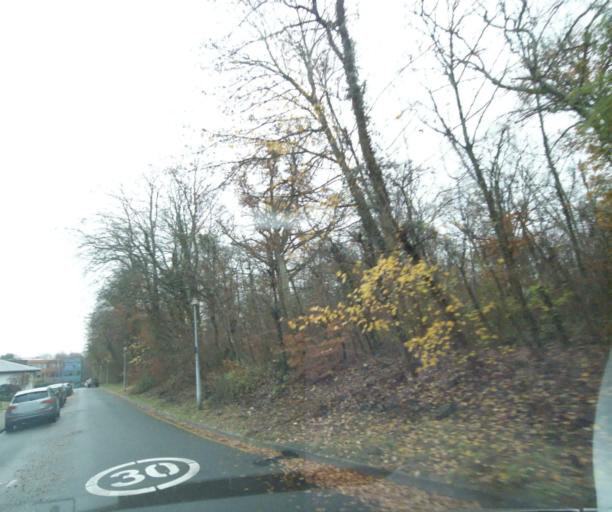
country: FR
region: Ile-de-France
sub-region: Departement de Seine-et-Marne
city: Avon
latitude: 48.4094
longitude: 2.7324
